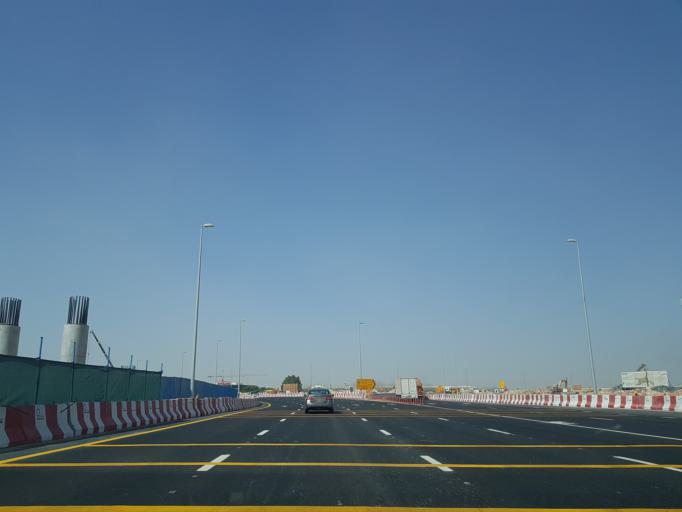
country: AE
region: Dubai
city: Dubai
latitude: 24.9661
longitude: 55.1841
